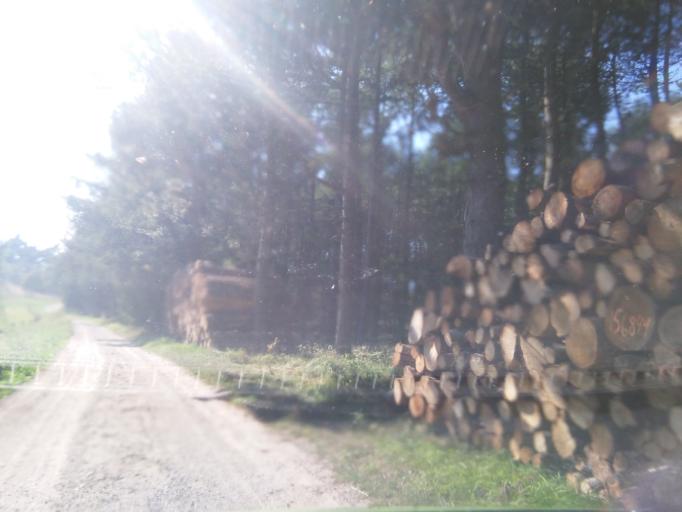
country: DK
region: Central Jutland
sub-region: Syddjurs Kommune
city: Ronde
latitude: 56.2080
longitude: 10.5225
